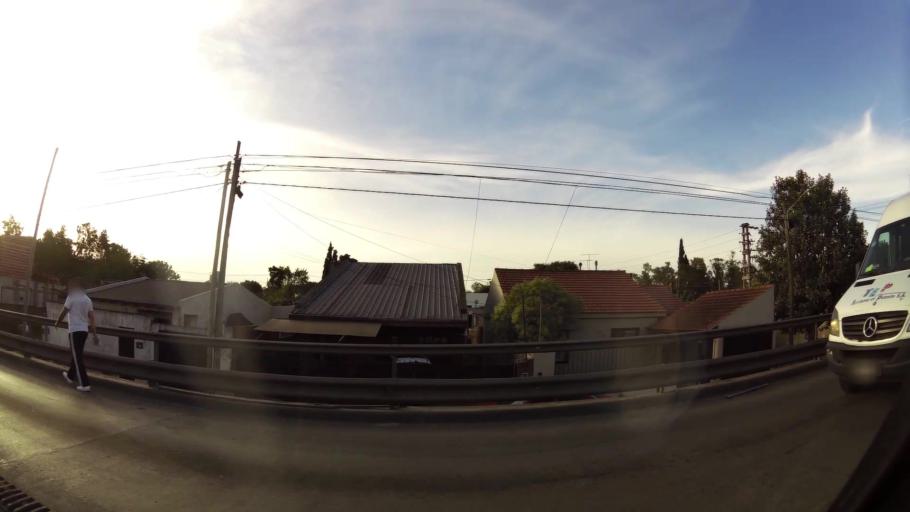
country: AR
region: Buenos Aires
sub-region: Partido de Almirante Brown
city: Adrogue
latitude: -34.8041
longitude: -58.3349
